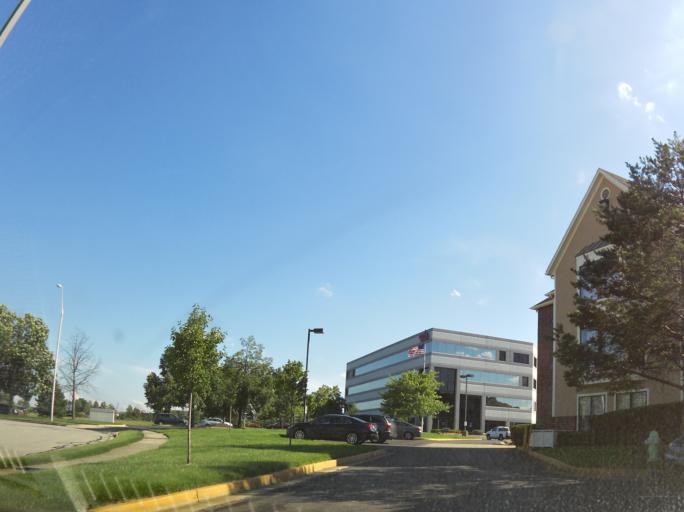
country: US
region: Ohio
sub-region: Greene County
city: Wright-Patterson AFB
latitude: 39.7772
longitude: -84.0556
